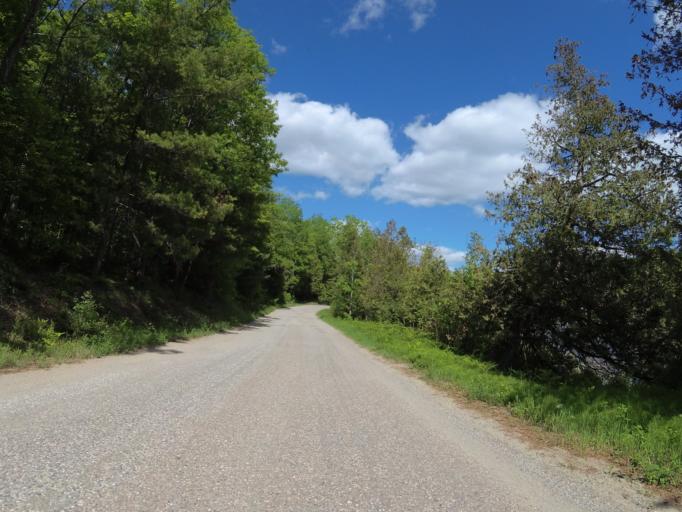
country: CA
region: Ontario
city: Renfrew
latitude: 45.0387
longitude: -76.8219
